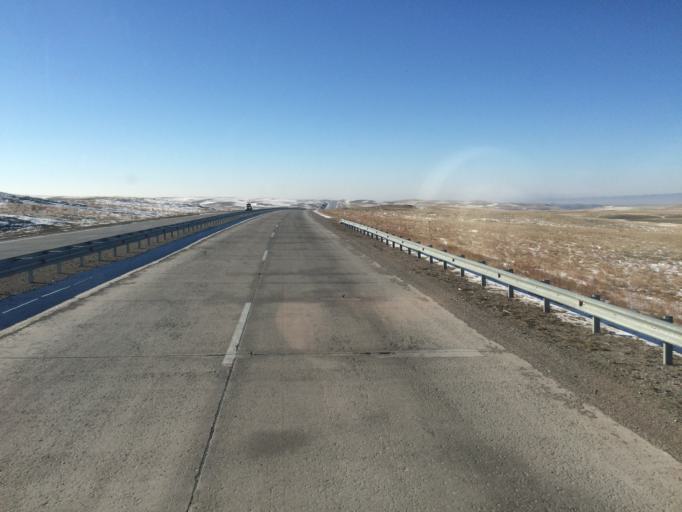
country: KZ
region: Zhambyl
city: Georgiyevka
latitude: 43.3649
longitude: 74.7142
